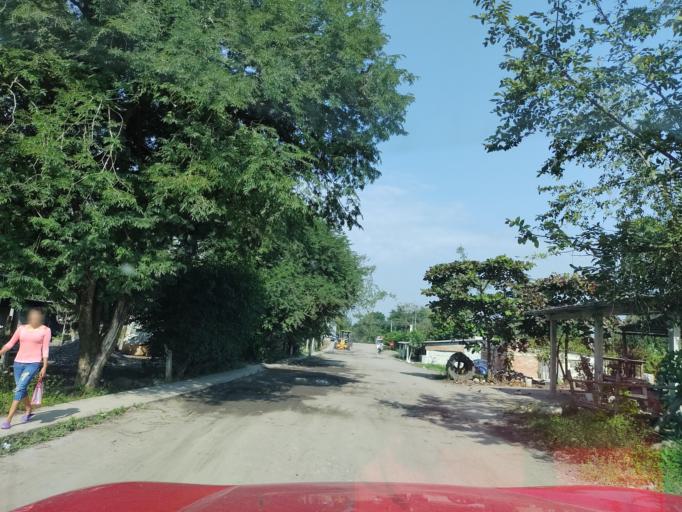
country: MX
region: Puebla
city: Espinal
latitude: 20.2730
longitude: -97.3318
